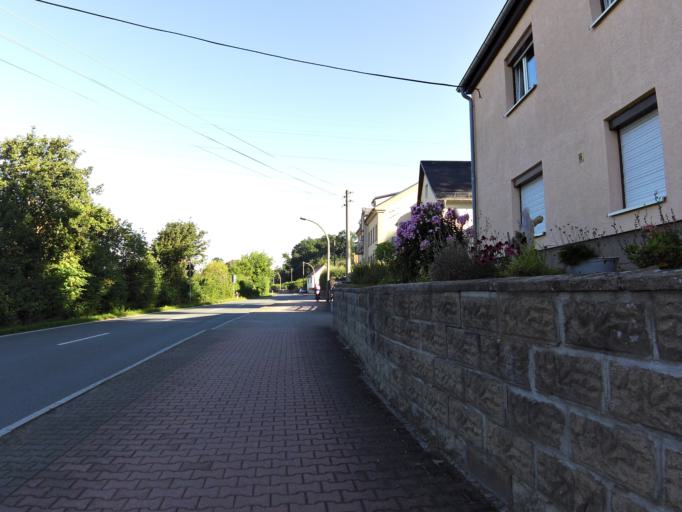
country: DE
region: Saxony
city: Weissig
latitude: 51.2430
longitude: 13.4147
